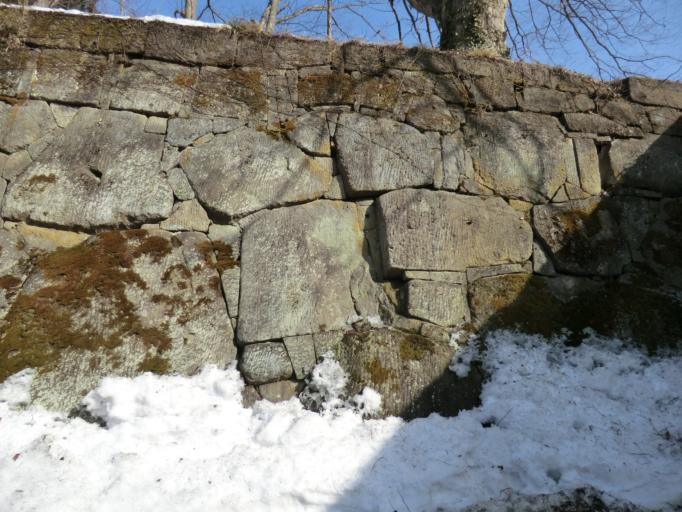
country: JP
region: Fukushima
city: Kitakata
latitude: 37.4882
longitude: 139.9298
